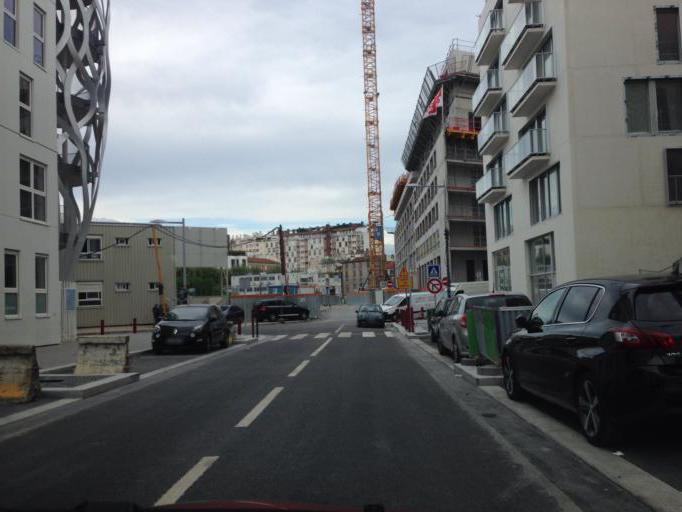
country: FR
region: Ile-de-France
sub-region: Departement des Hauts-de-Seine
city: Boulogne-Billancourt
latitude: 48.8258
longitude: 2.2415
